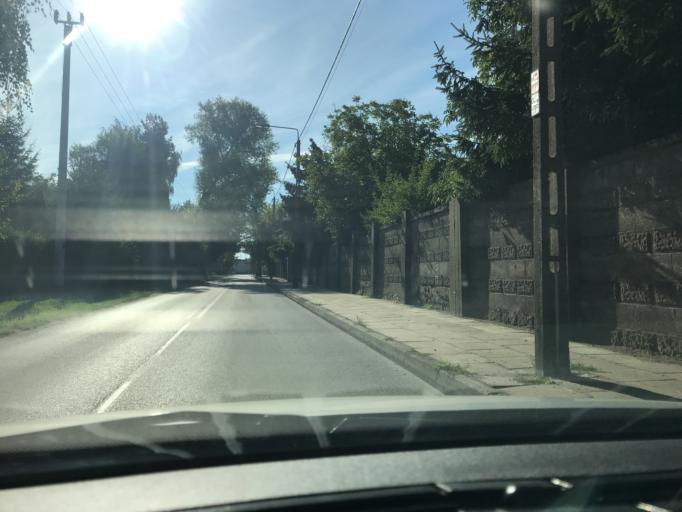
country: PL
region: Masovian Voivodeship
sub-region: Powiat pruszkowski
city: Piastow
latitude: 52.1691
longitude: 20.8358
